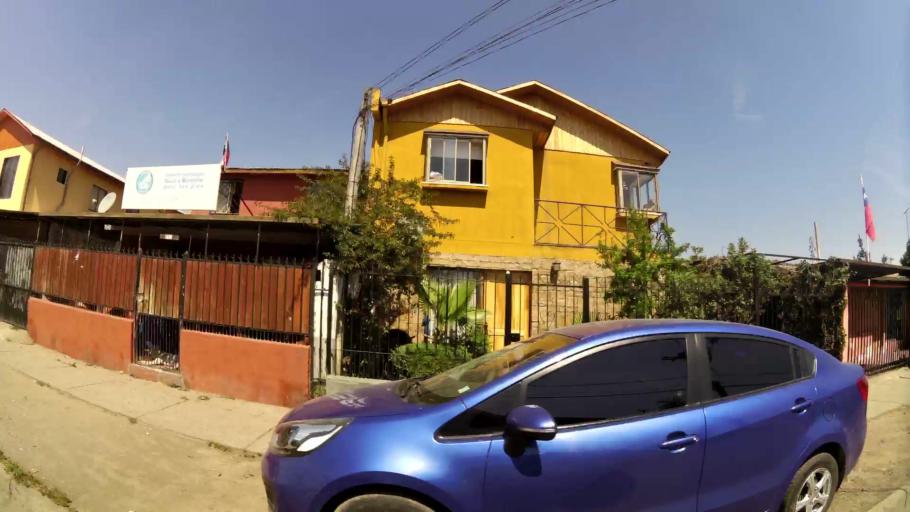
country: CL
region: Santiago Metropolitan
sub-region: Provincia de Santiago
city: La Pintana
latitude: -33.5456
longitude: -70.6476
